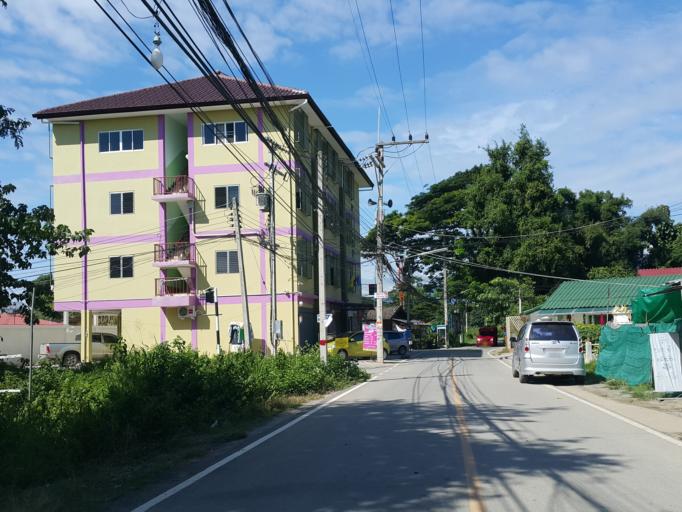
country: TH
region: Chiang Mai
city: San Sai
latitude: 18.8105
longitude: 99.0368
